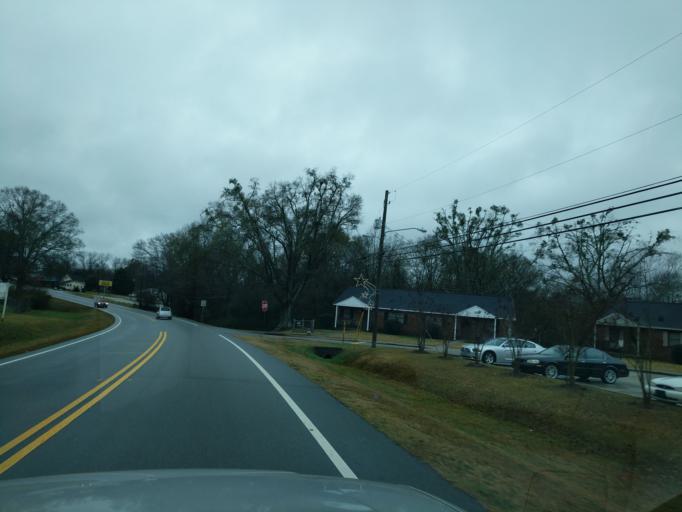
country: US
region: Georgia
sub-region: Hart County
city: Royston
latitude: 34.3496
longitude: -83.1118
